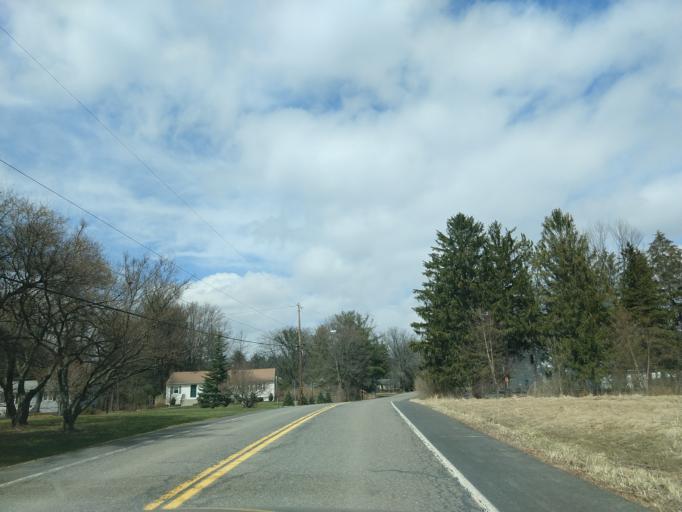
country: US
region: New York
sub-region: Tompkins County
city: Northeast Ithaca
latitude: 42.4652
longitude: -76.4669
